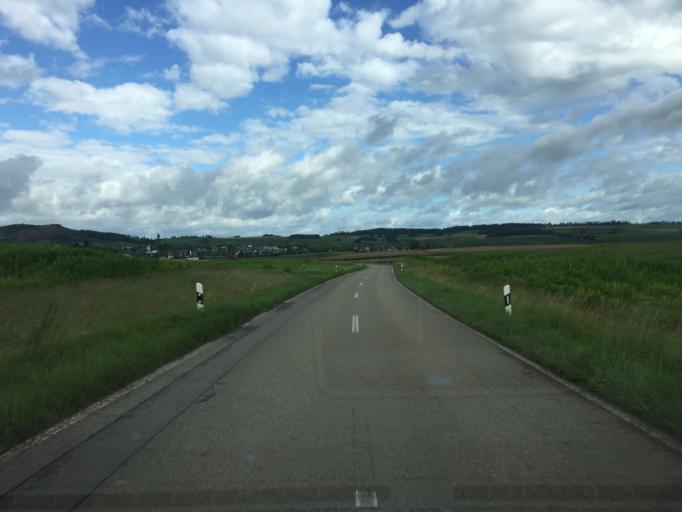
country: CH
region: Schaffhausen
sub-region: Bezirk Unterklettgau
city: Wilchingen
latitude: 47.6527
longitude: 8.4467
